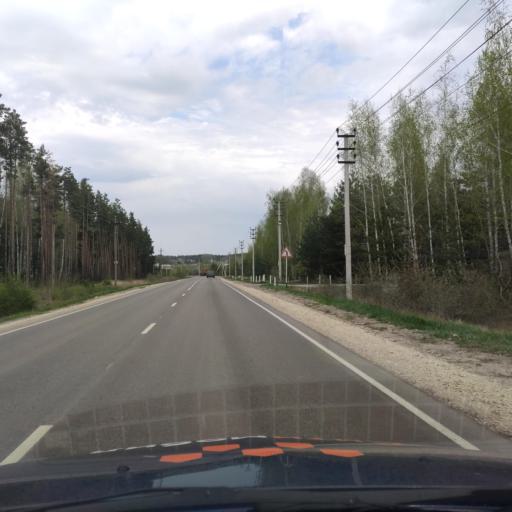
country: RU
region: Voronezj
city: Podgornoye
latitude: 51.8641
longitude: 39.1691
